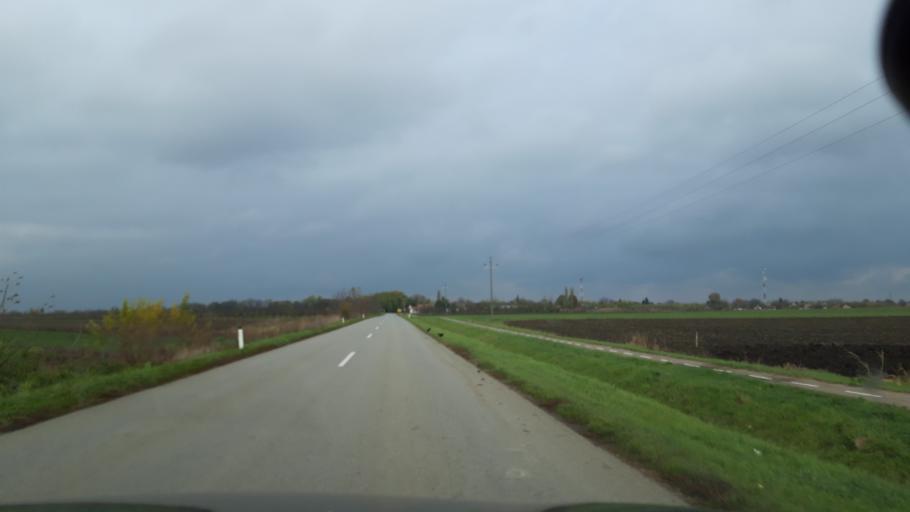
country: HU
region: Csongrad
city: Roszke
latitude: 46.1468
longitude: 20.1013
